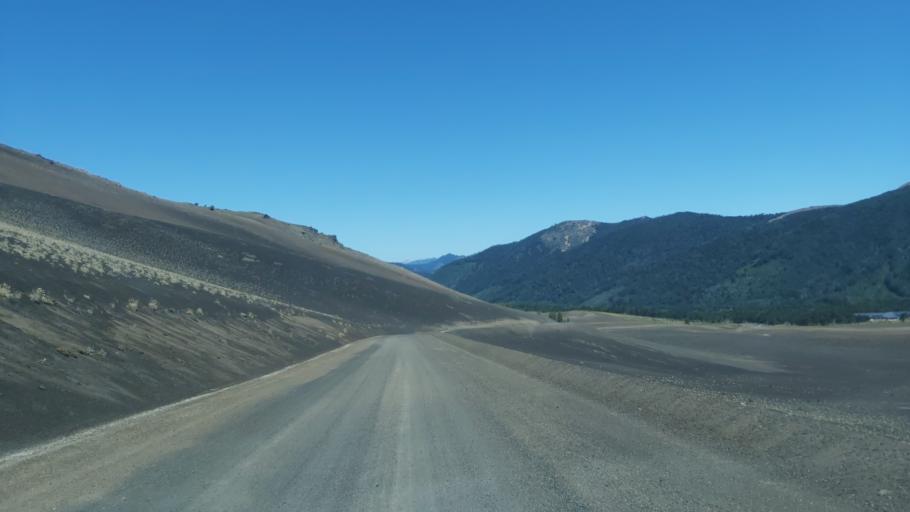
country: CL
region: Araucania
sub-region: Provincia de Cautin
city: Vilcun
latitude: -38.4069
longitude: -71.5428
